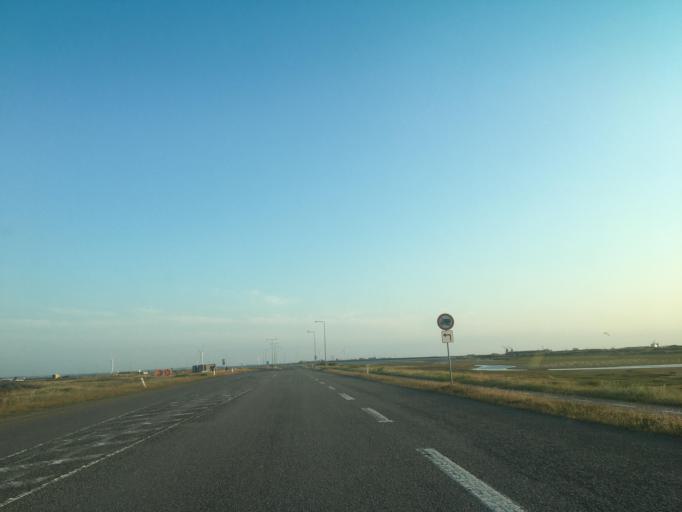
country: DK
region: Central Jutland
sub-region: Lemvig Kommune
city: Thyboron
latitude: 56.7055
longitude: 8.2467
